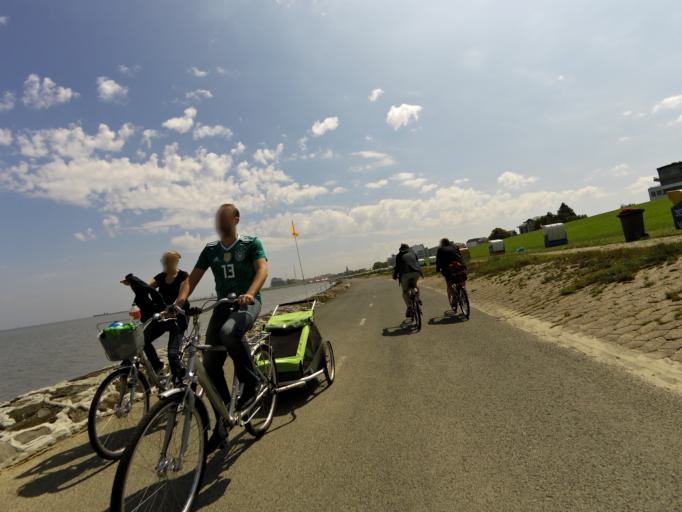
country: DE
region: Lower Saxony
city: Cuxhaven
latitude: 53.8809
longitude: 8.6857
